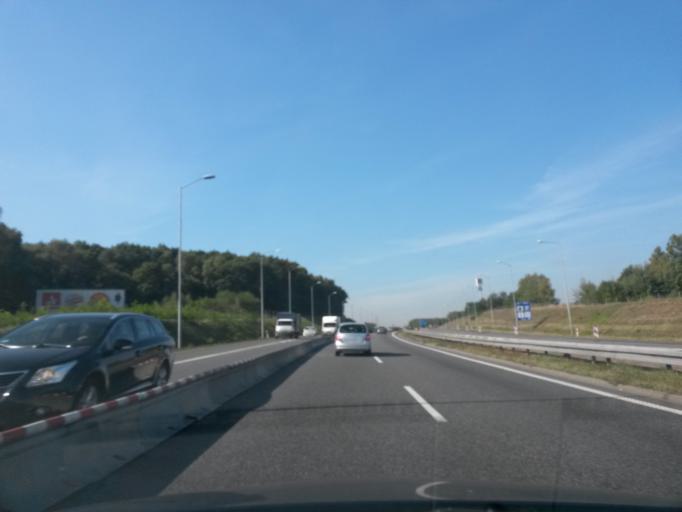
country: PL
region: Silesian Voivodeship
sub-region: Ruda Slaska
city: Ruda Slaska
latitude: 50.2487
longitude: 18.8888
